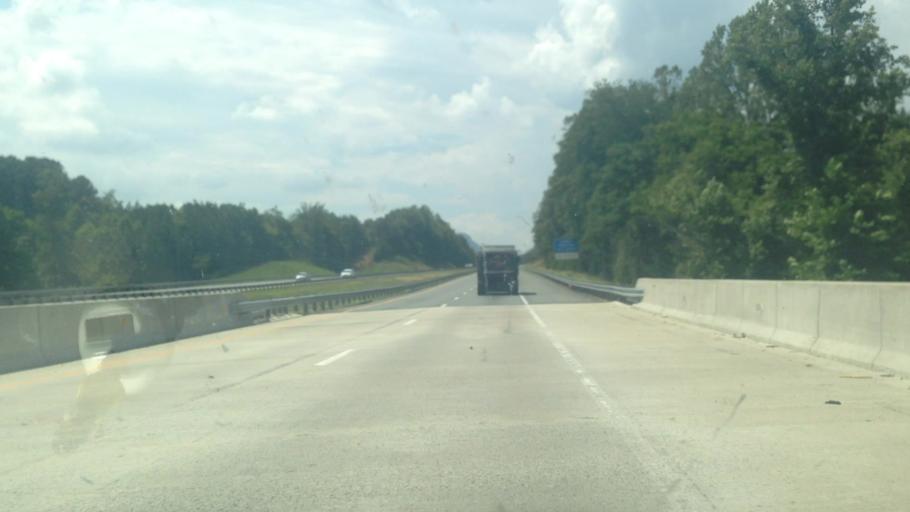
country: US
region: North Carolina
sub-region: Stokes County
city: King
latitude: 36.3022
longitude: -80.4158
